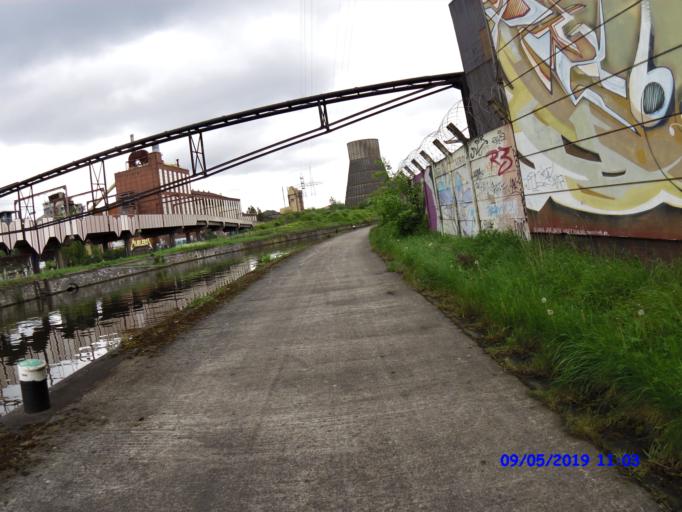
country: BE
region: Wallonia
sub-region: Province du Hainaut
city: Charleroi
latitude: 50.4123
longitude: 4.4069
